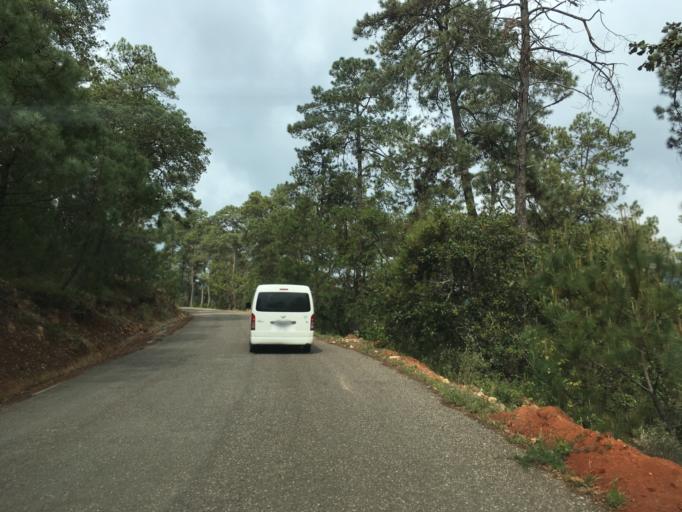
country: MX
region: Oaxaca
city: Santiago Tilantongo
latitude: 17.2124
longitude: -97.2797
